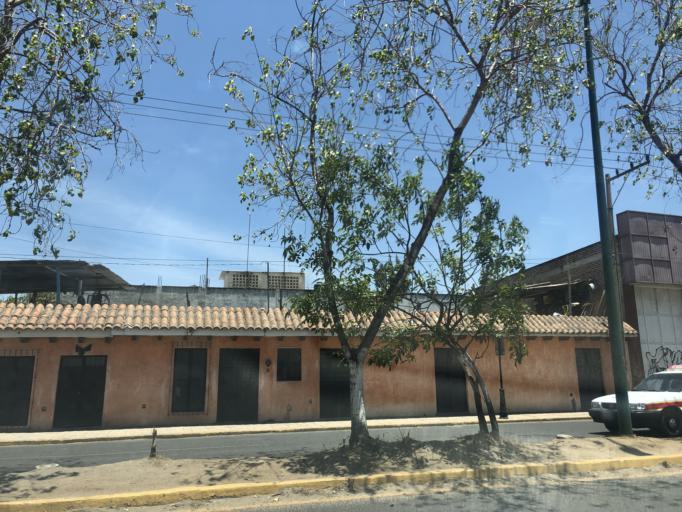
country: MX
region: Chiapas
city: San Cristobal de las Casas
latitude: 16.7210
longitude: -92.6363
